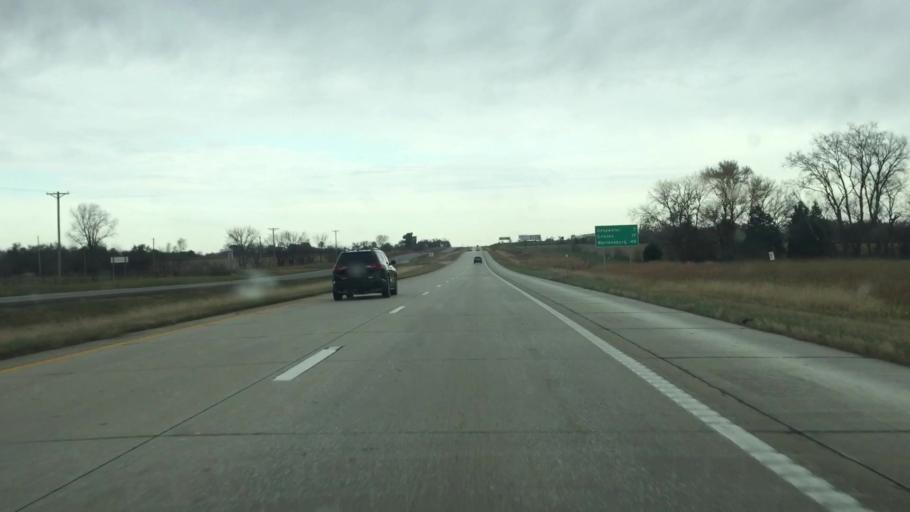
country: US
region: Missouri
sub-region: Saint Clair County
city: Osceola
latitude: 38.1567
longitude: -93.7224
